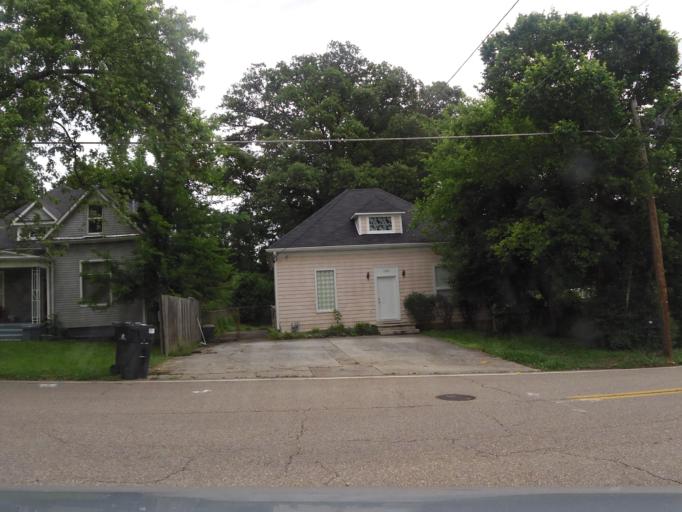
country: US
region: Tennessee
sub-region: Knox County
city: Knoxville
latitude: 35.9649
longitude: -83.9585
